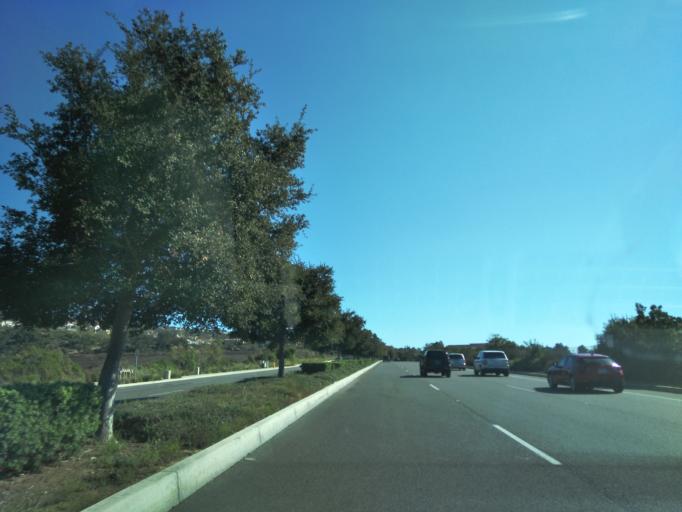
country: US
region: California
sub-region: Orange County
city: San Joaquin Hills
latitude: 33.6124
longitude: -117.8258
